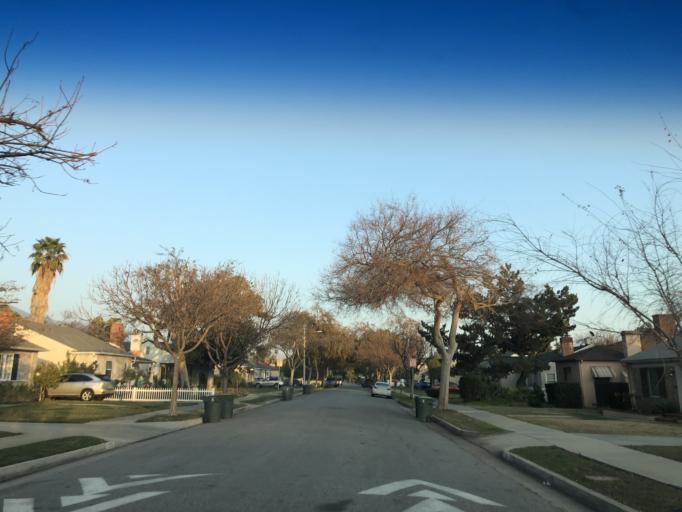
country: US
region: California
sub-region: Los Angeles County
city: East Pasadena
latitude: 34.1535
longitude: -118.1151
